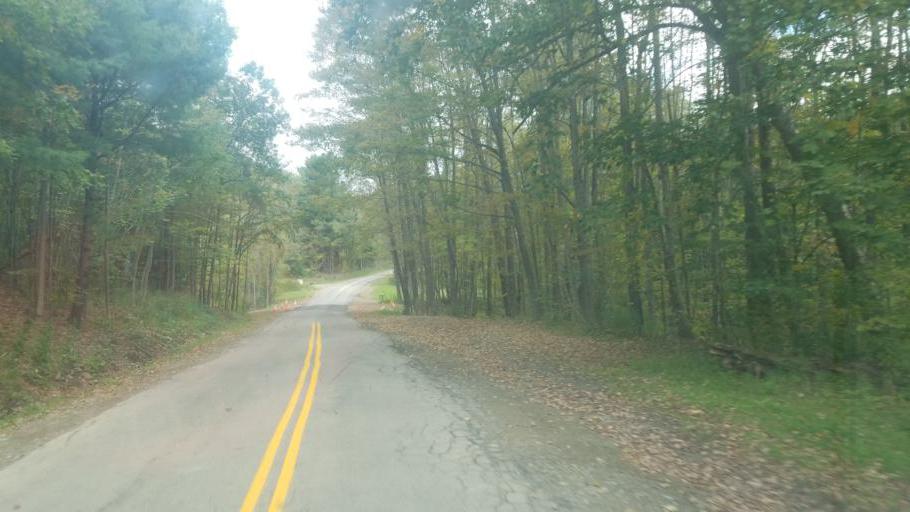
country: US
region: New York
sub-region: Allegany County
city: Cuba
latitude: 42.2192
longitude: -78.3611
